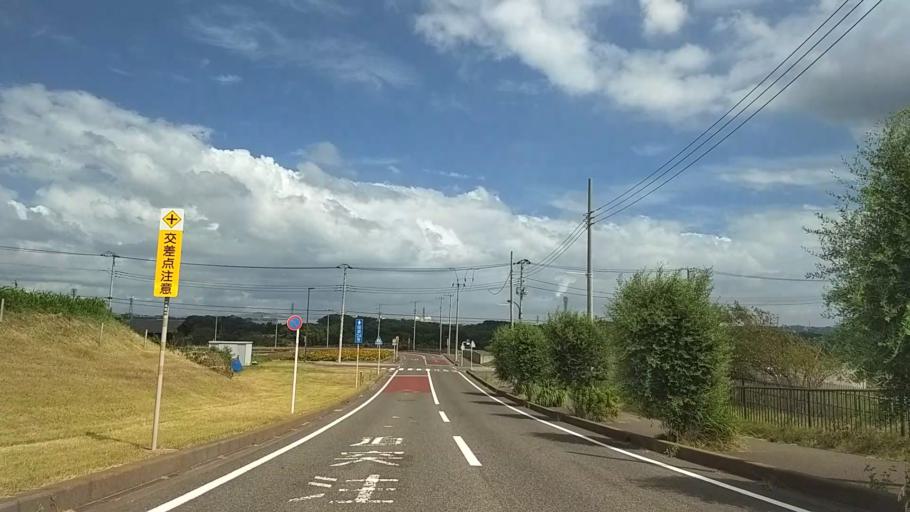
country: JP
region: Kanagawa
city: Miura
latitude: 35.1957
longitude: 139.6140
